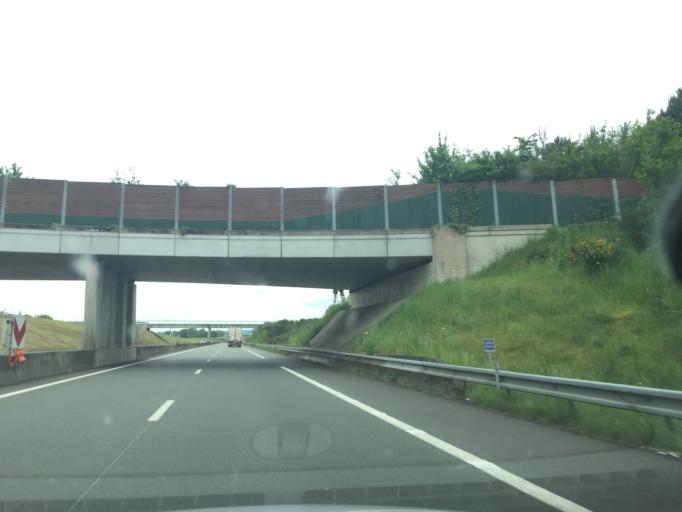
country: FR
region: Pays de la Loire
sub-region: Departement de la Sarthe
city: Luceau
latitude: 47.6964
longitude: 0.3578
